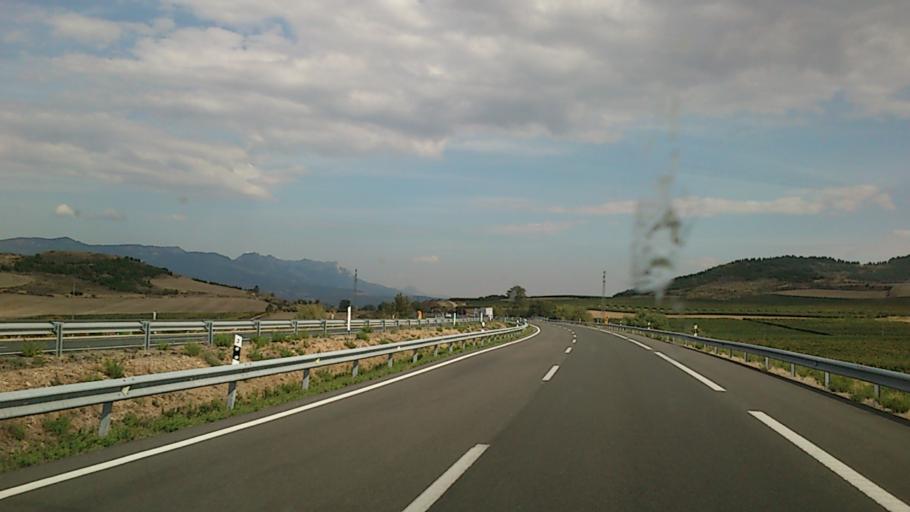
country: ES
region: La Rioja
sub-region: Provincia de La Rioja
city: Ollauri
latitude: 42.5361
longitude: -2.8278
